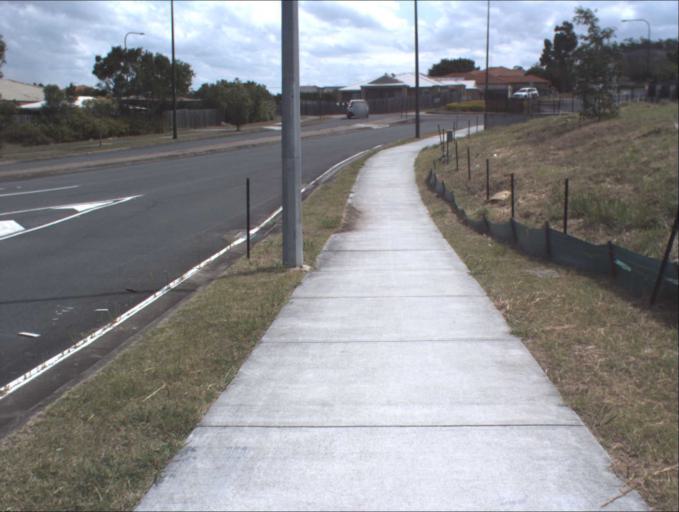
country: AU
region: Queensland
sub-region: Logan
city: Springwood
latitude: -27.6119
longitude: 153.1124
